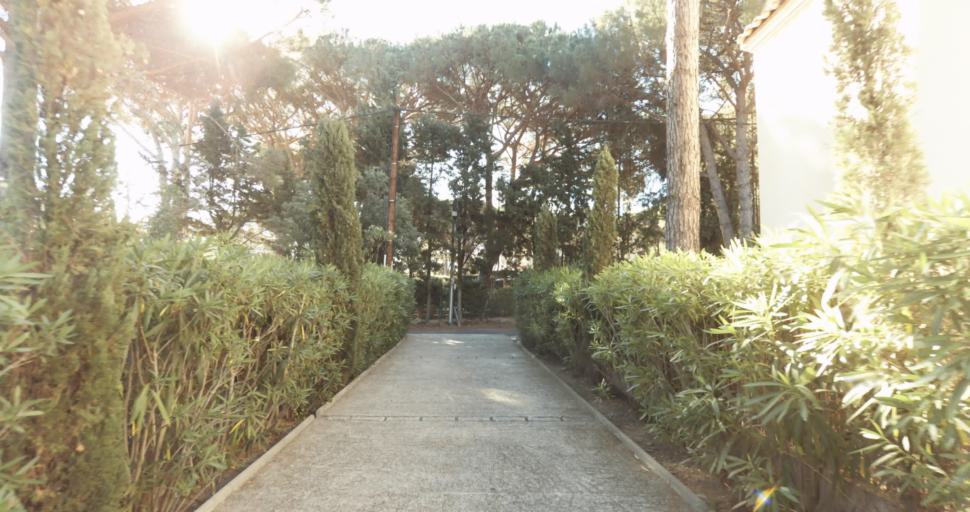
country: FR
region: Provence-Alpes-Cote d'Azur
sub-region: Departement du Var
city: Saint-Tropez
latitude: 43.2595
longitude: 6.6255
